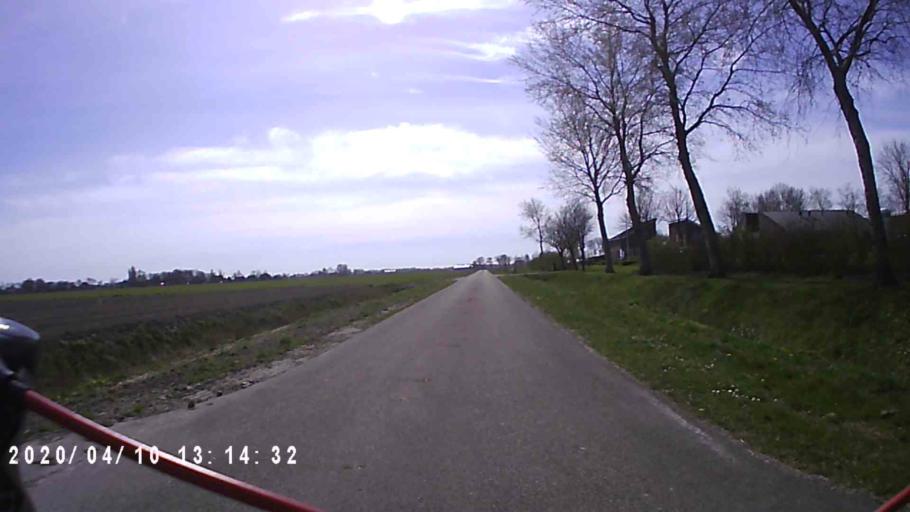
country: NL
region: Groningen
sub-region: Gemeente De Marne
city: Ulrum
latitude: 53.4001
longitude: 6.4173
